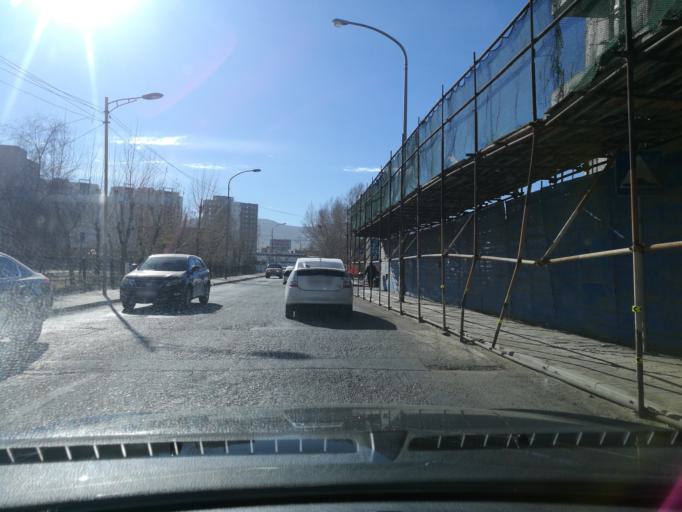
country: MN
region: Ulaanbaatar
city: Ulaanbaatar
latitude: 47.9102
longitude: 106.9074
